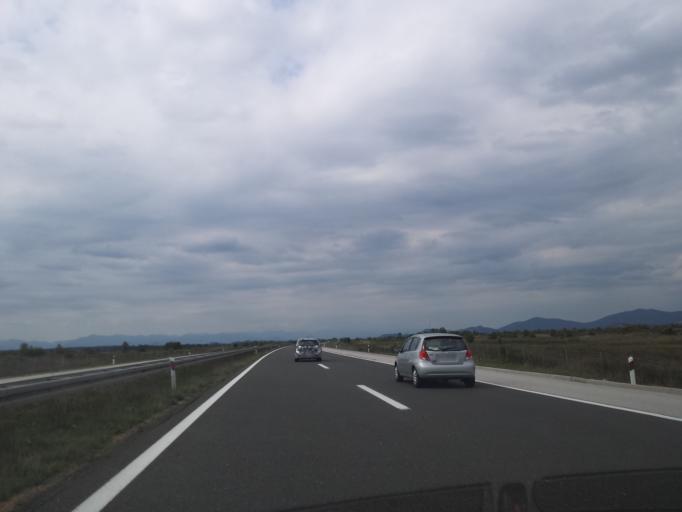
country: HR
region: Licko-Senjska
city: Gospic
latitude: 44.4819
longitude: 15.5570
